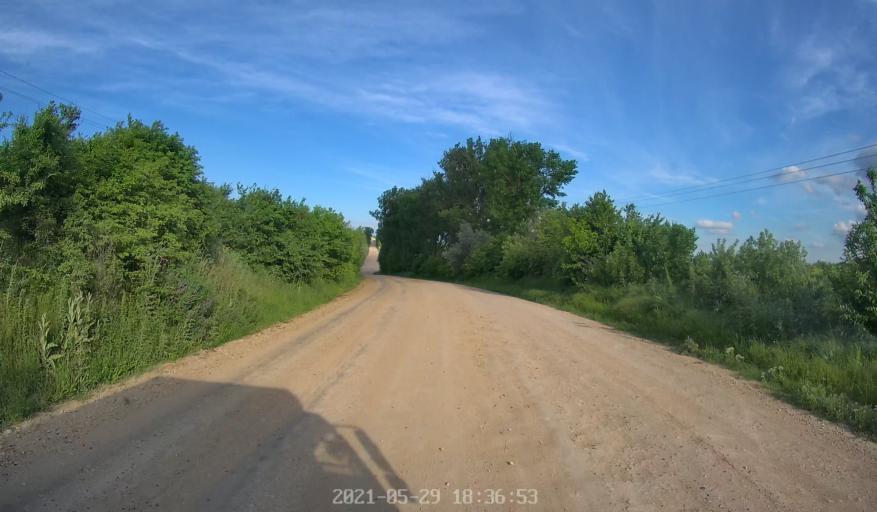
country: MD
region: Chisinau
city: Singera
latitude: 46.8053
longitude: 28.9271
